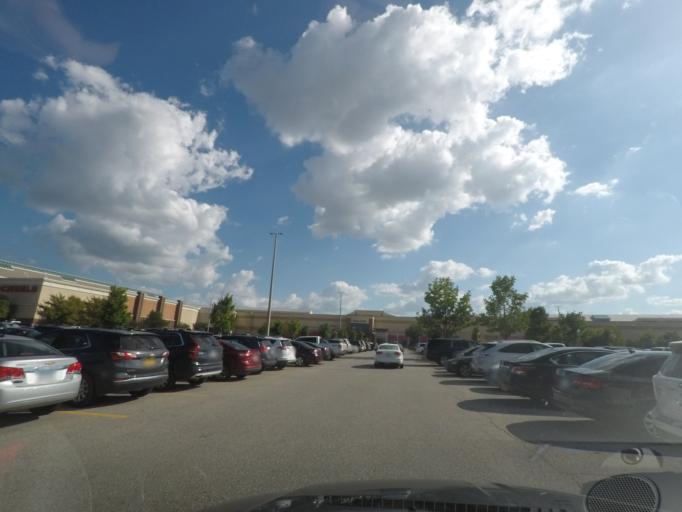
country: US
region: Iowa
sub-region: Polk County
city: Clive
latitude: 41.5718
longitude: -93.8050
